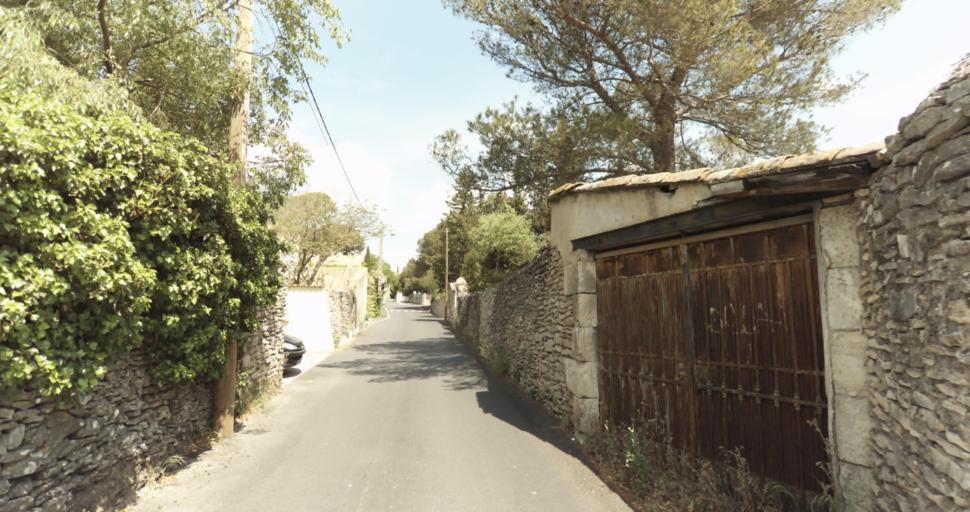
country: FR
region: Languedoc-Roussillon
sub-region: Departement du Gard
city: Nimes
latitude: 43.8540
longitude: 4.3483
